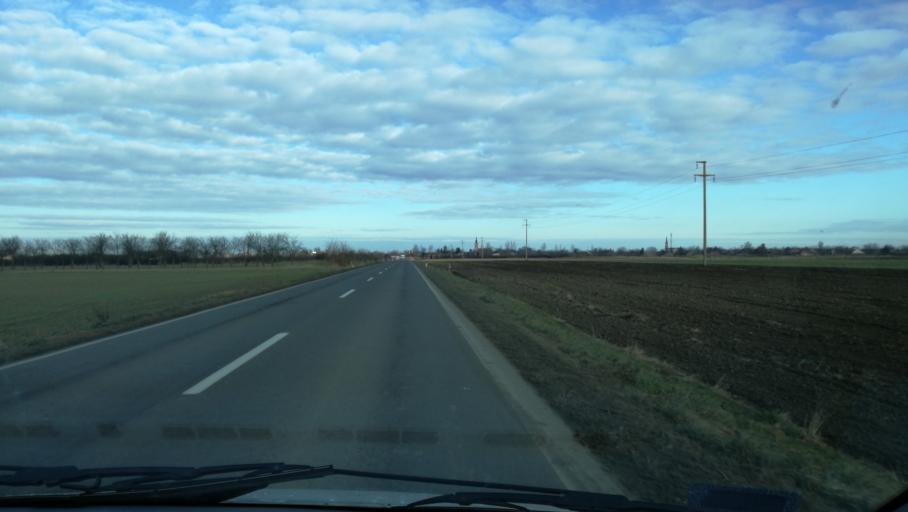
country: RS
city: Ostojicevo
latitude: 45.8779
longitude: 20.1651
